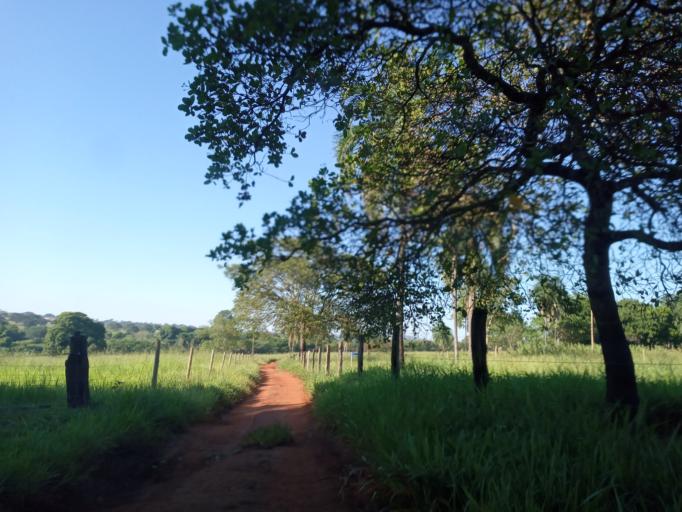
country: BR
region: Minas Gerais
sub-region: Ituiutaba
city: Ituiutaba
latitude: -18.9754
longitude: -49.4958
